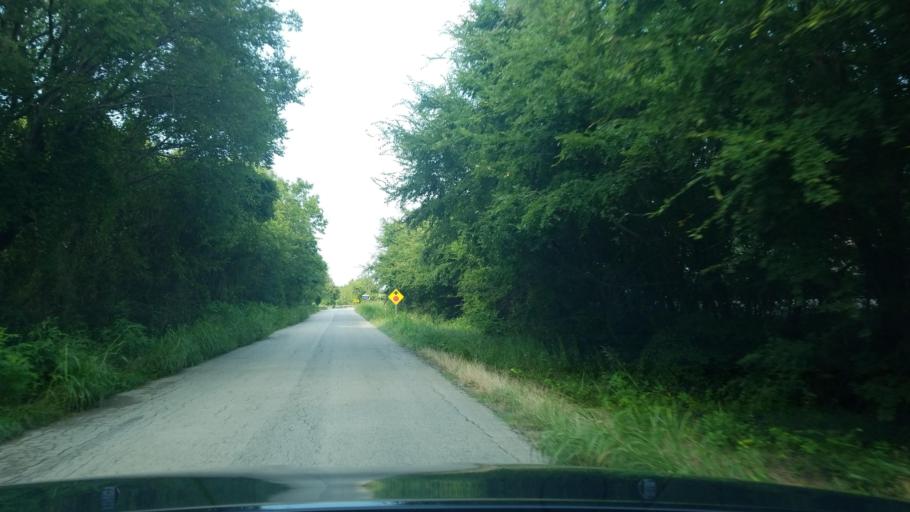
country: US
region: Texas
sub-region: Denton County
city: Cross Roads
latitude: 33.2462
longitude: -97.0636
